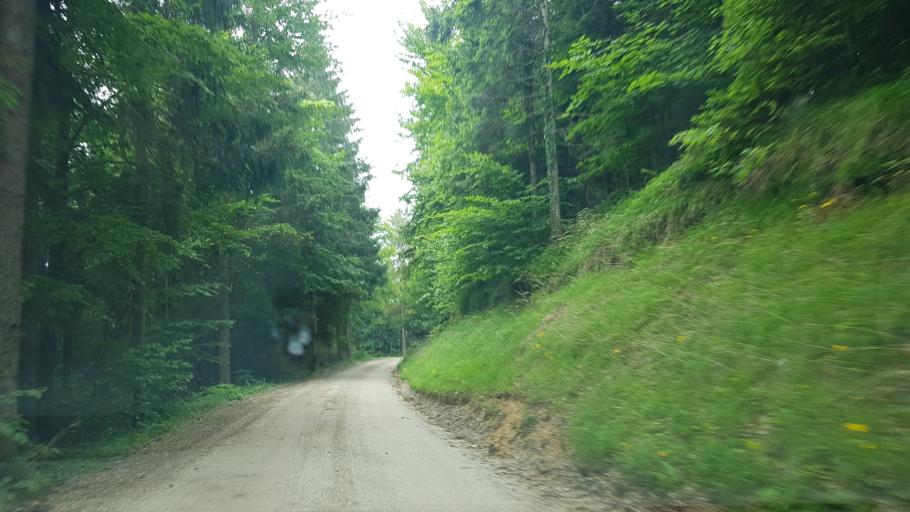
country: SI
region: Dobrna
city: Dobrna
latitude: 46.3719
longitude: 15.2484
